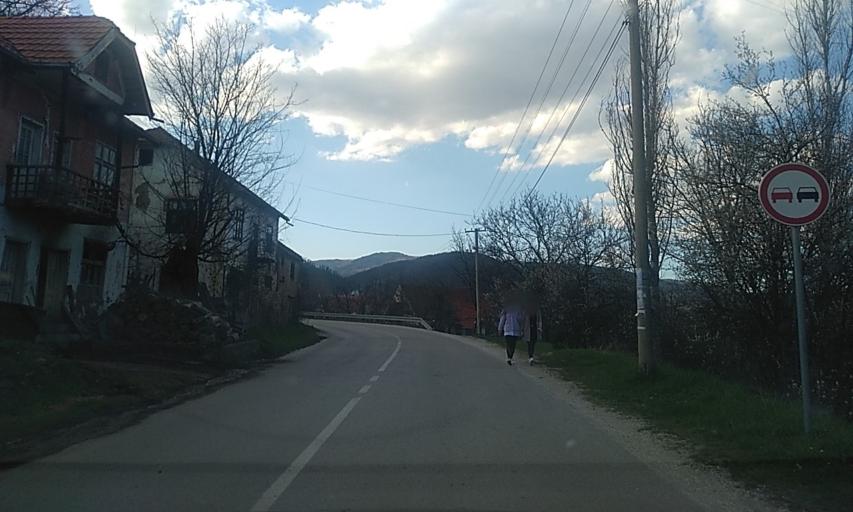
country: RS
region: Central Serbia
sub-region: Pcinjski Okrug
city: Bosilegrad
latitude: 42.4813
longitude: 22.4765
